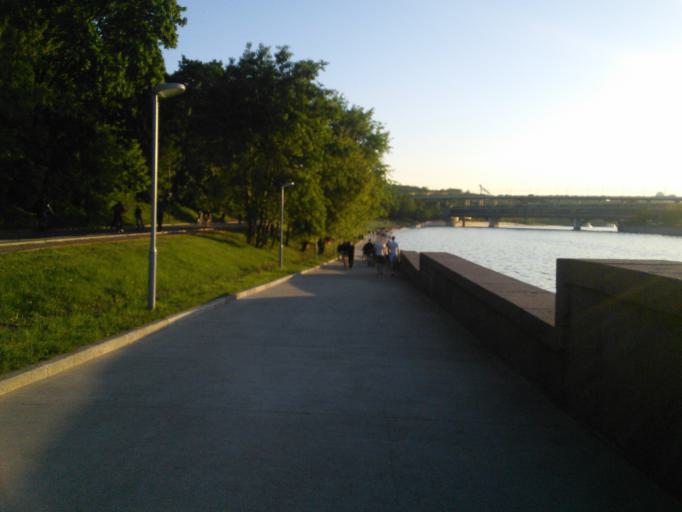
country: RU
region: Moskovskaya
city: Leninskiye Gory
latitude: 55.7108
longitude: 37.5691
